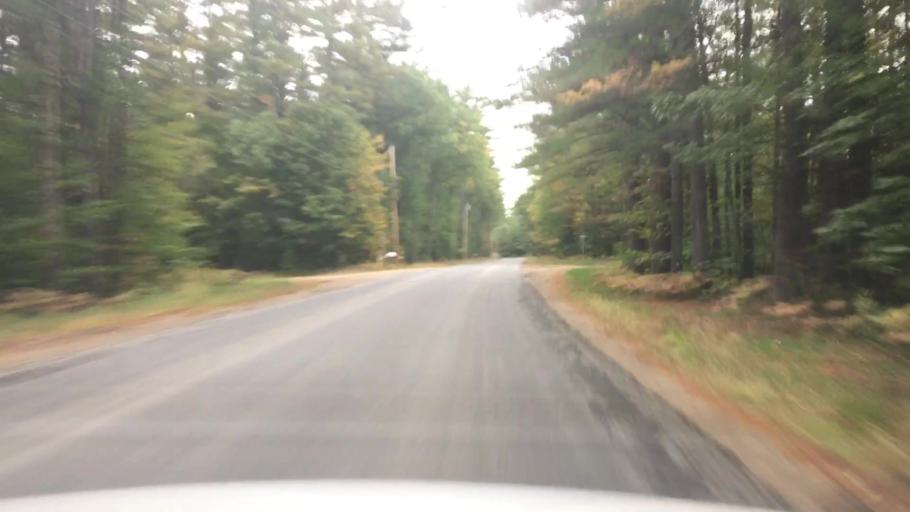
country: US
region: Maine
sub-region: Oxford County
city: Bethel
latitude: 44.4448
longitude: -70.7948
